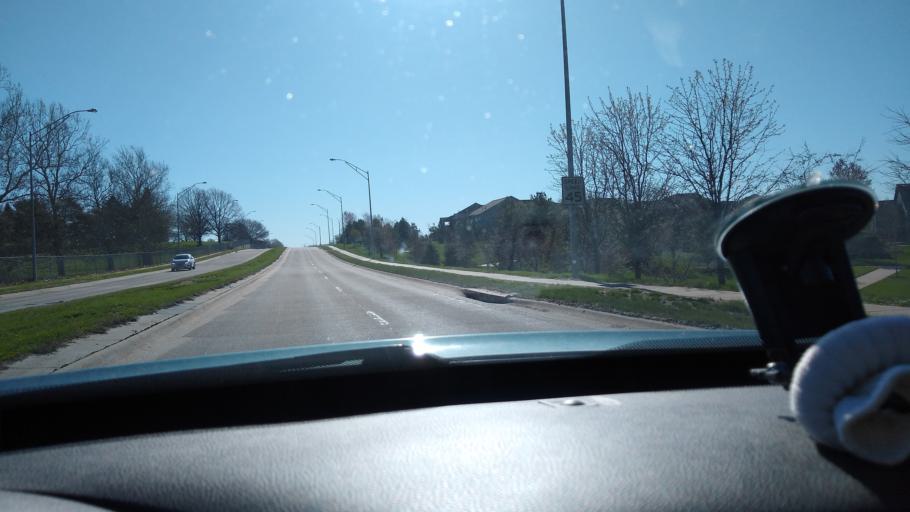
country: US
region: Nebraska
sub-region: Douglas County
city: Ralston
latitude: 41.1908
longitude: -96.0705
